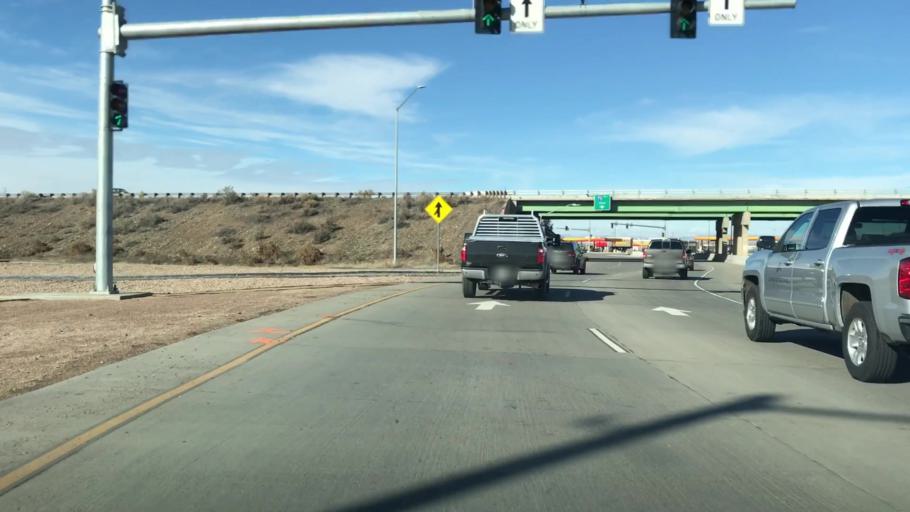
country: US
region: Colorado
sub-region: Mesa County
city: Redlands
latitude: 39.1113
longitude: -108.6436
